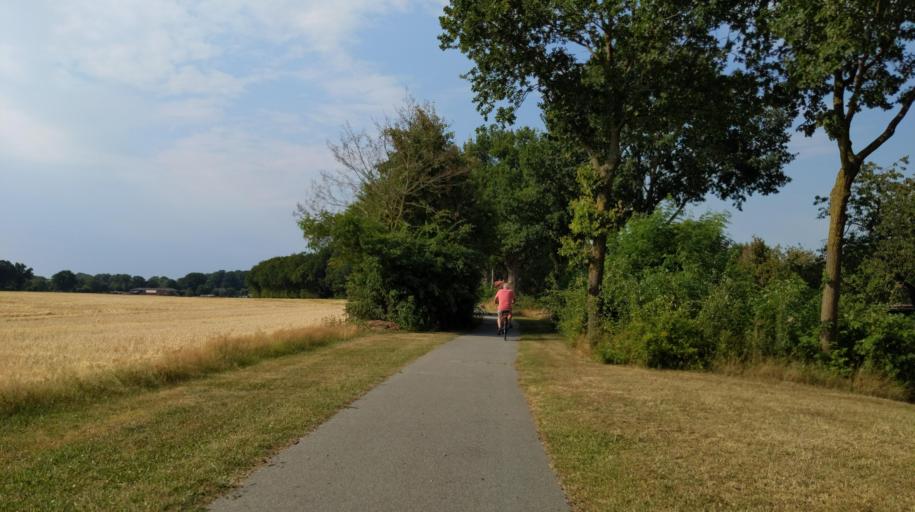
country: DE
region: Schleswig-Holstein
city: Rondeshagen
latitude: 53.7437
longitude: 10.6368
